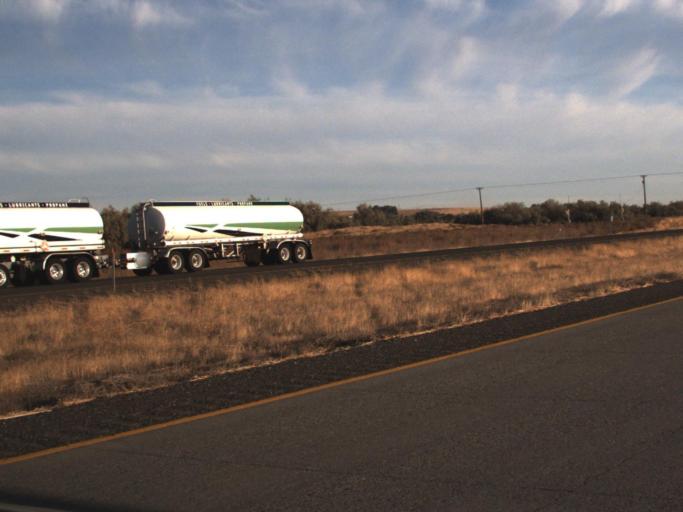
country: US
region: Washington
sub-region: Franklin County
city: Pasco
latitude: 46.3840
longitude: -119.0691
